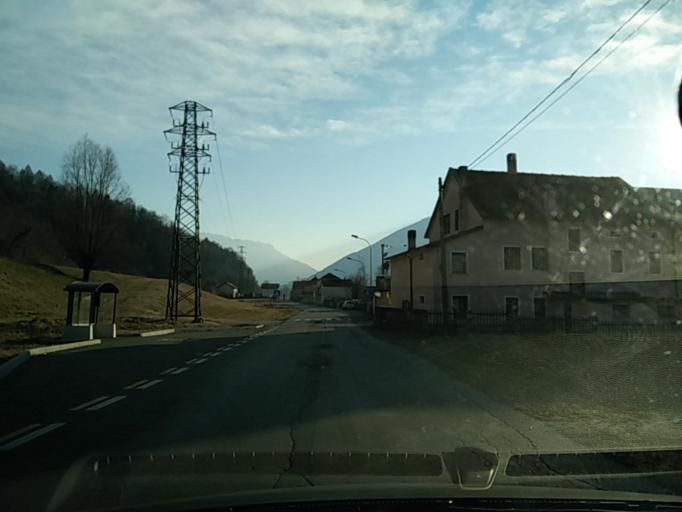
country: IT
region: Veneto
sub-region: Provincia di Belluno
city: Puos d'Alpago
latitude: 46.1430
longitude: 12.3297
